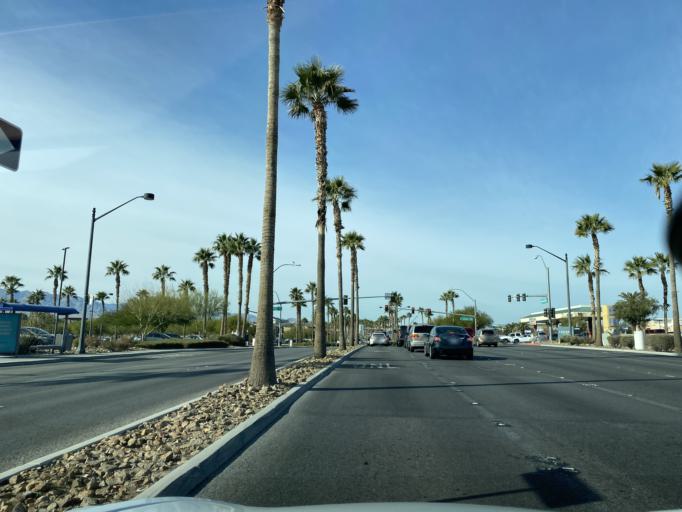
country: US
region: Nevada
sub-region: Clark County
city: Las Vegas
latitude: 36.2711
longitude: -115.2638
